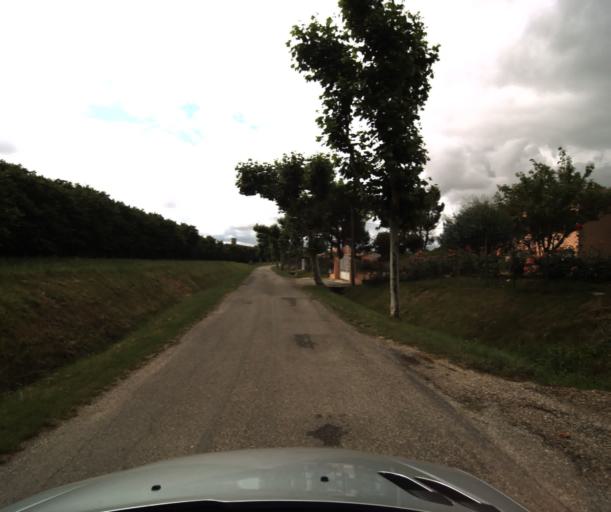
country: FR
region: Midi-Pyrenees
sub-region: Departement du Tarn-et-Garonne
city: Lavit
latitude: 43.9631
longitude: 0.9186
